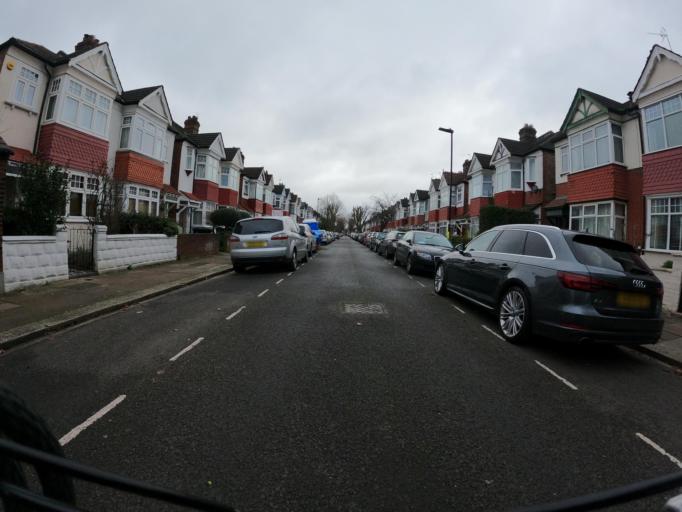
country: GB
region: England
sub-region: Greater London
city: Ealing
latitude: 51.5080
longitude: -0.3237
